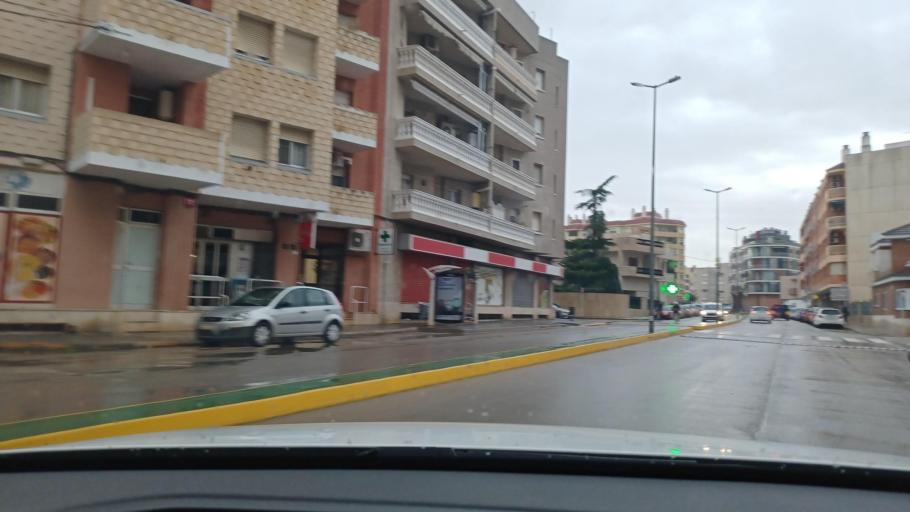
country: ES
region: Catalonia
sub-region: Provincia de Tarragona
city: Amposta
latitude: 40.7047
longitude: 0.5784
